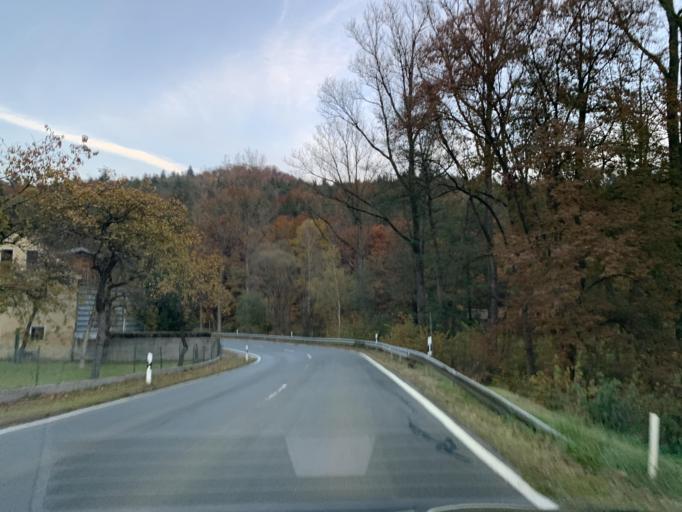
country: DE
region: Bavaria
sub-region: Upper Palatinate
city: Bach
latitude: 49.3805
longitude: 12.3793
